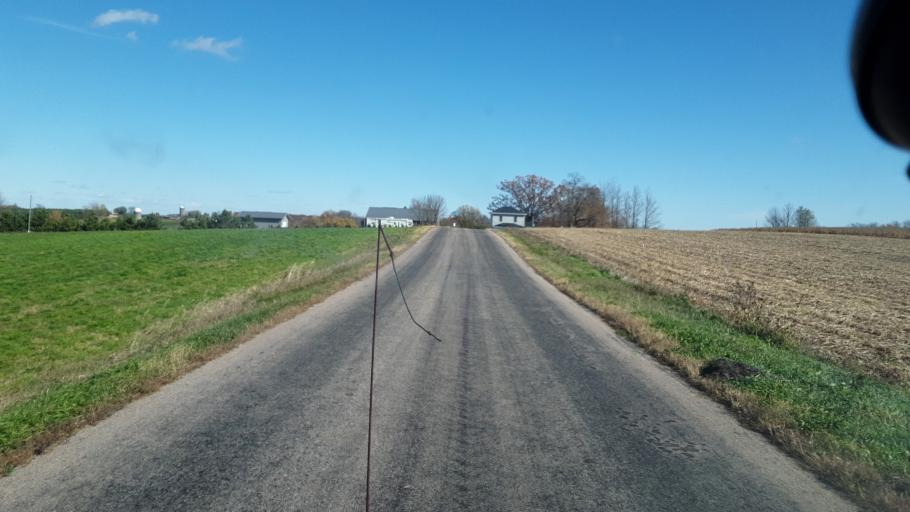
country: US
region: Wisconsin
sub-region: Vernon County
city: Hillsboro
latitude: 43.6969
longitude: -90.4446
